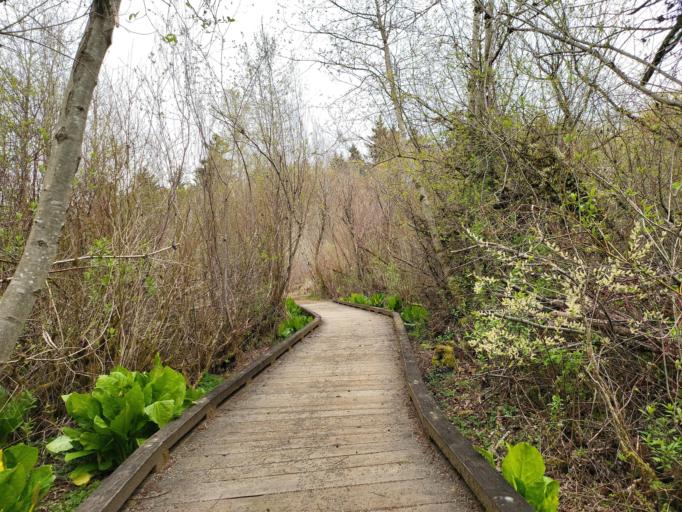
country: US
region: Washington
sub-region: King County
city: Newport
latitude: 47.5931
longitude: -122.1856
